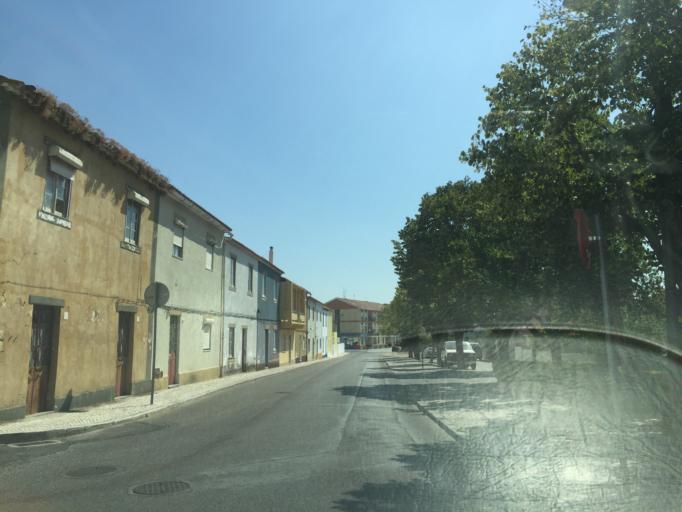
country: PT
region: Santarem
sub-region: Chamusca
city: Vila Nova da Barquinha
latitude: 39.4616
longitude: -8.4400
